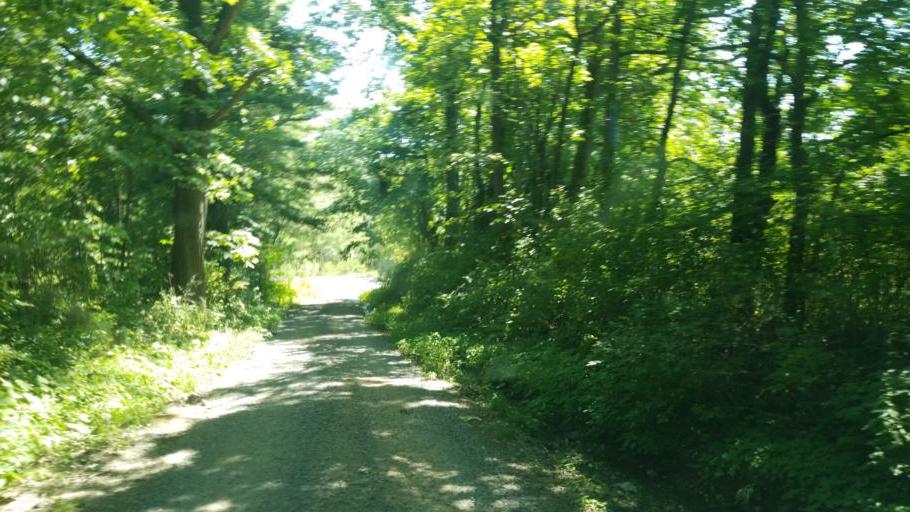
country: US
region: Pennsylvania
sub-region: Clarion County
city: Knox
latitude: 41.1923
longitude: -79.6489
